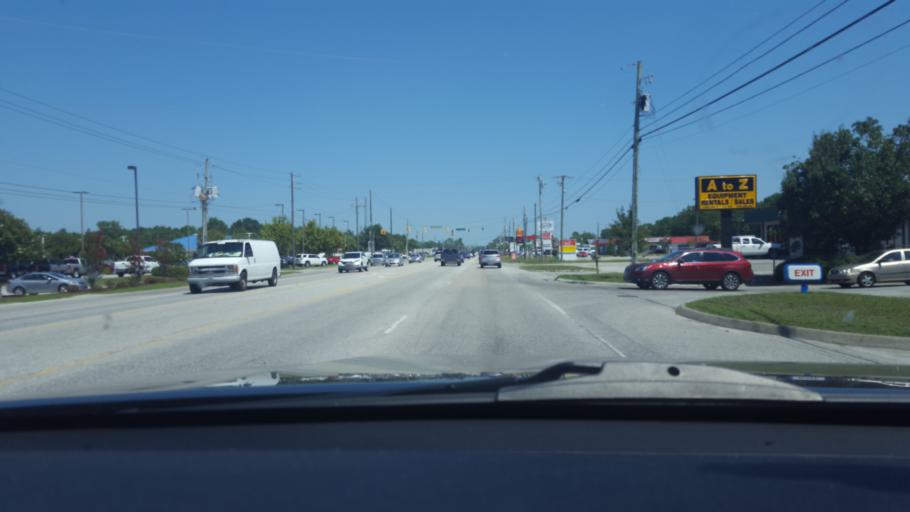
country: US
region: North Carolina
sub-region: New Hanover County
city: Kings Grant
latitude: 34.2545
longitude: -77.8463
